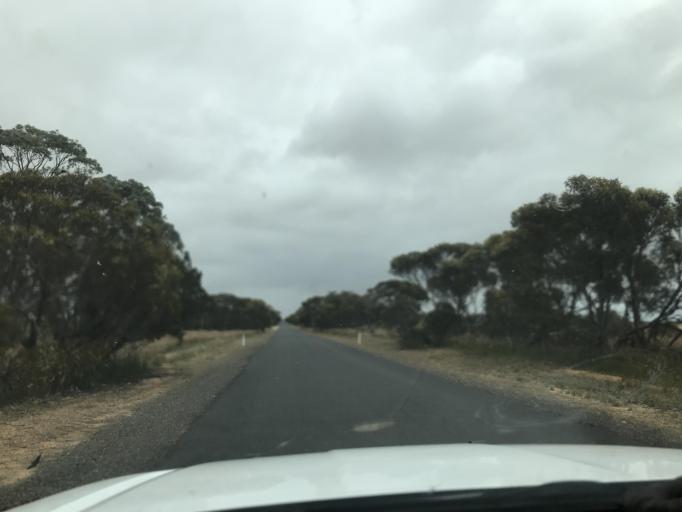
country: AU
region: South Australia
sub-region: Tatiara
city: Bordertown
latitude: -36.1209
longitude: 141.0674
